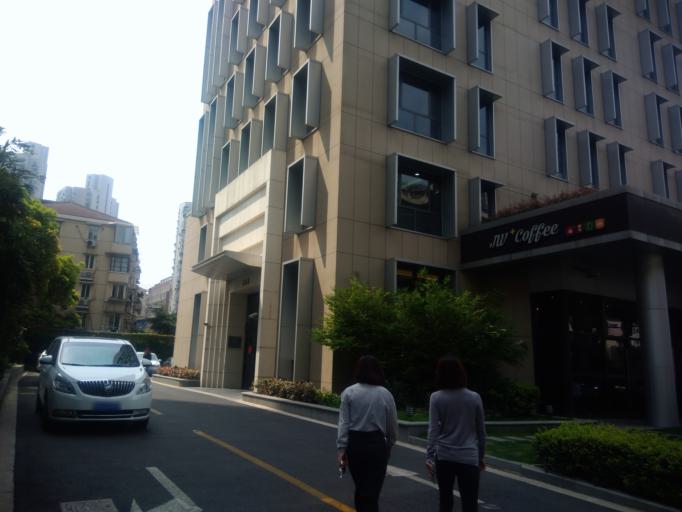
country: CN
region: Shanghai Shi
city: Luwan
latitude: 31.2006
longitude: 121.4720
